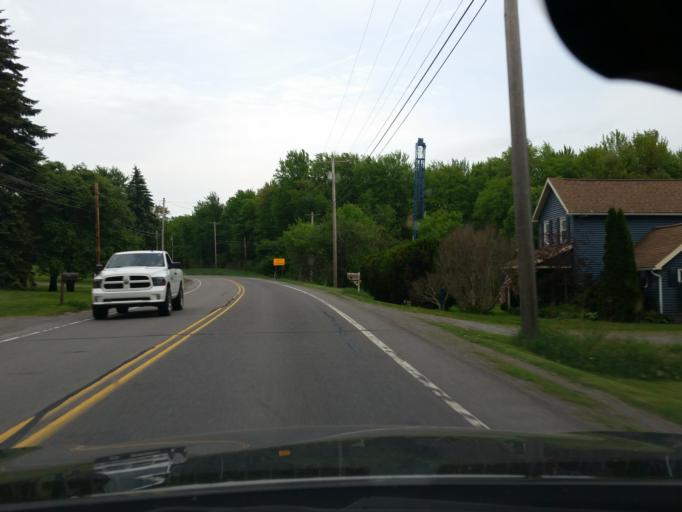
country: US
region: Pennsylvania
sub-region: Elk County
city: Ridgway
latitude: 41.3996
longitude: -78.7007
